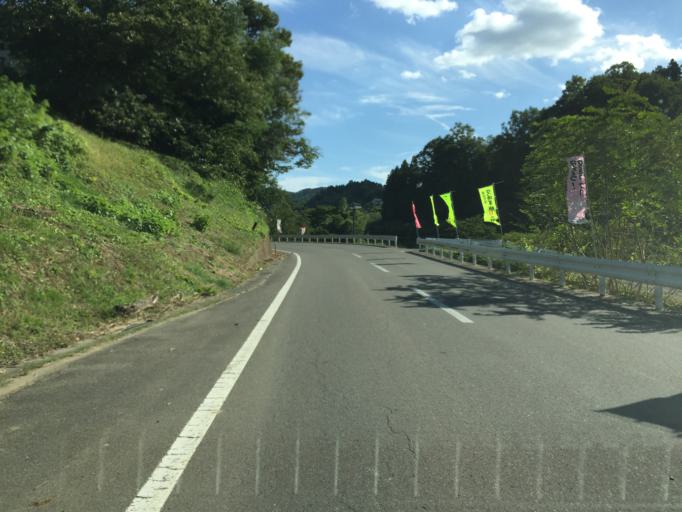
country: JP
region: Fukushima
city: Yanagawamachi-saiwaicho
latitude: 37.8475
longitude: 140.6531
